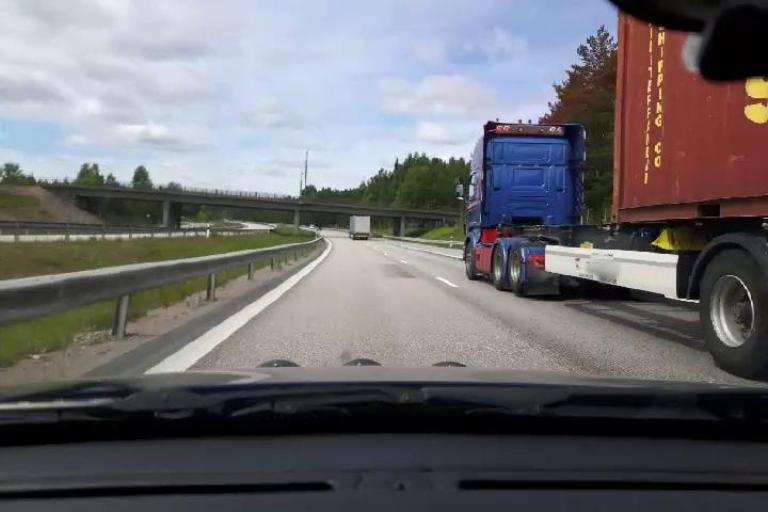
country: SE
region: Uppsala
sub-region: Alvkarleby Kommun
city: AElvkarleby
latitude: 60.4665
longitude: 17.4087
